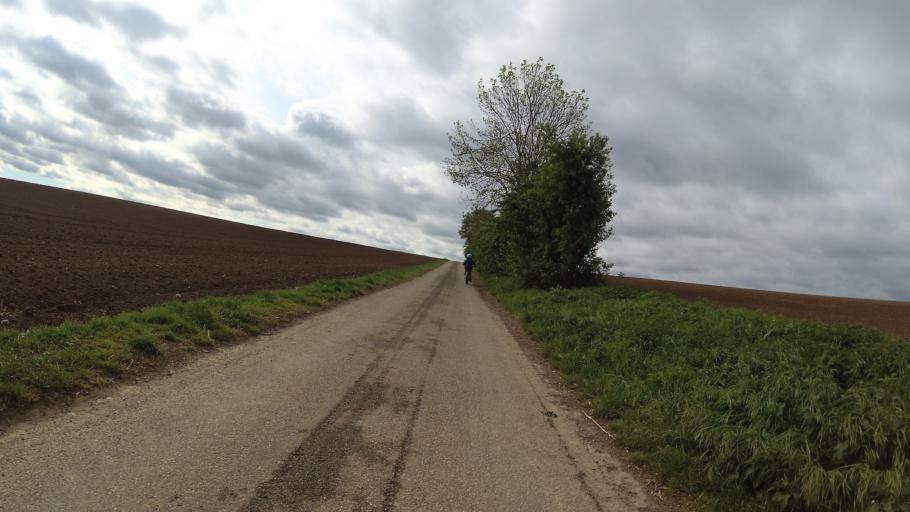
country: DE
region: Baden-Wuerttemberg
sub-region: Regierungsbezirk Stuttgart
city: Oedheim
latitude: 49.2182
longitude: 9.2609
